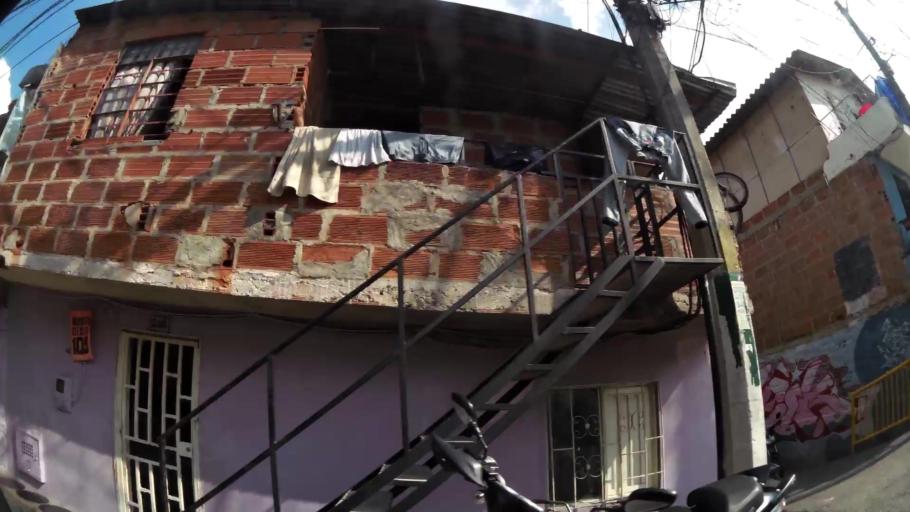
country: CO
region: Antioquia
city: Medellin
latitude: 6.2820
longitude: -75.5759
